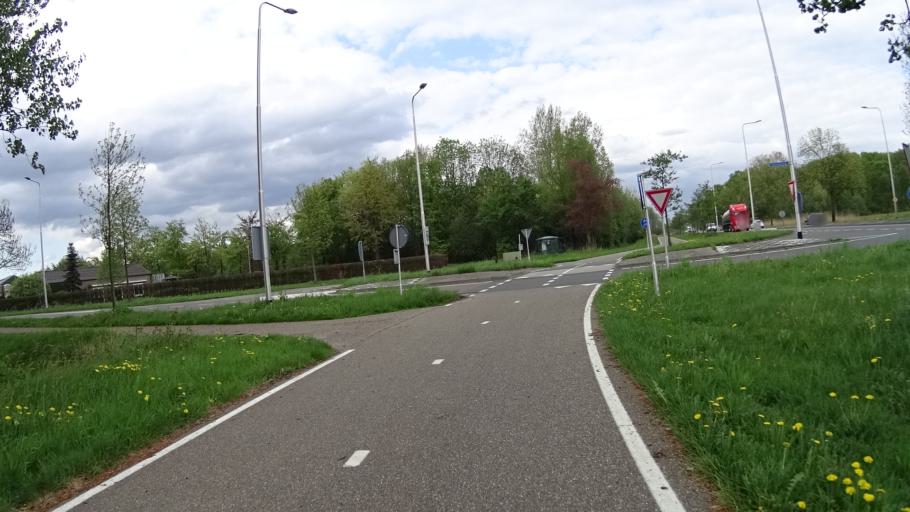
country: NL
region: North Brabant
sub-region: Gemeente Laarbeek
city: Aarle-Rixtel
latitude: 51.5396
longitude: 5.6643
